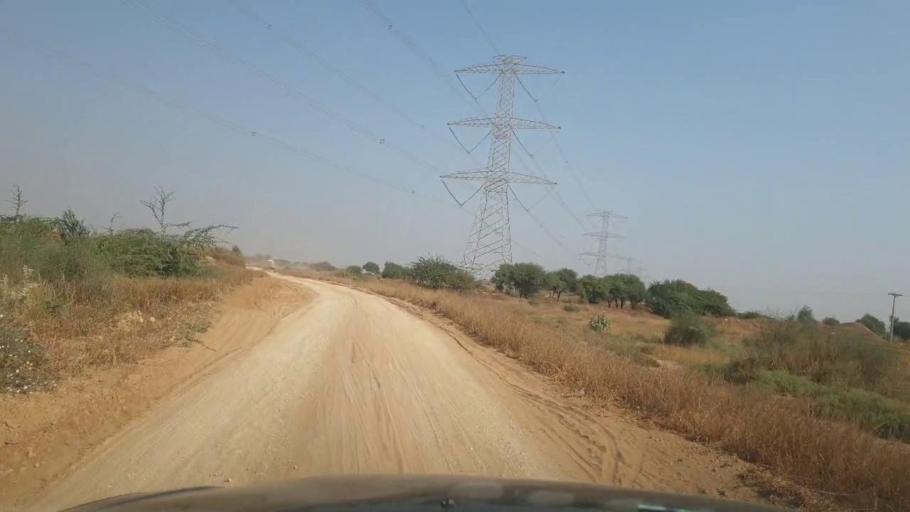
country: PK
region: Sindh
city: Gharo
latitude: 25.2353
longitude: 67.6812
